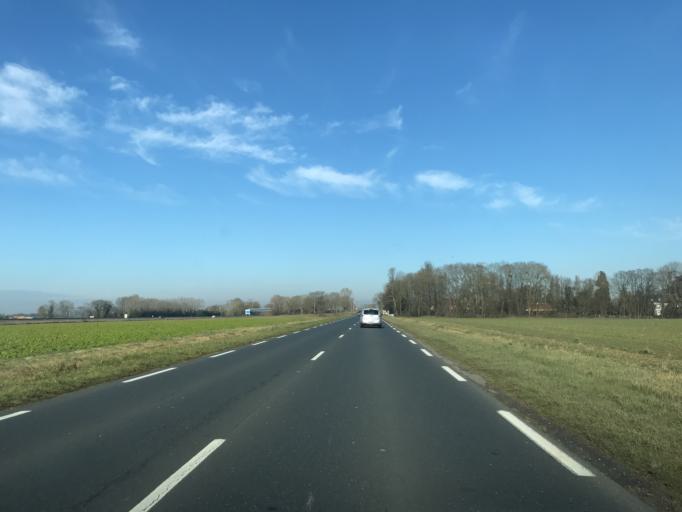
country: FR
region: Haute-Normandie
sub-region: Departement de l'Eure
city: Saint-Pierre-du-Vauvray
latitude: 49.2158
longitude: 1.2183
